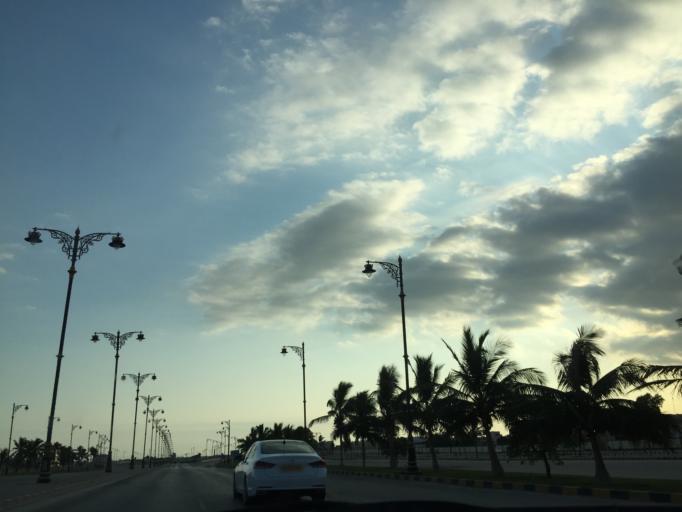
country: OM
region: Zufar
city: Salalah
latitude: 17.0388
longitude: 54.0607
